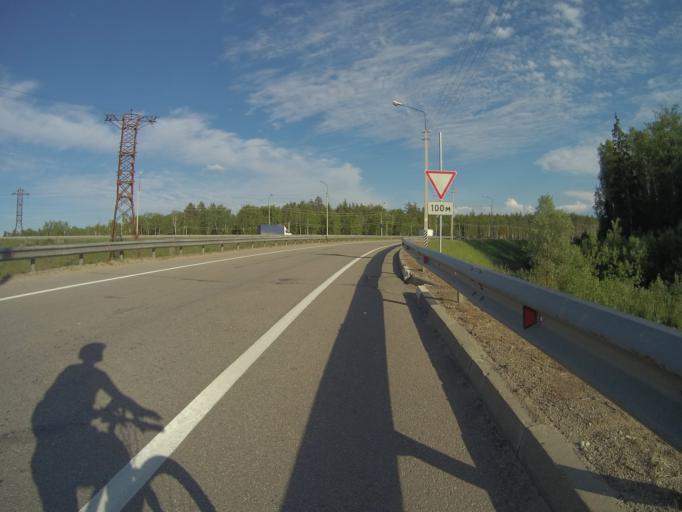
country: RU
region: Vladimir
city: Kameshkovo
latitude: 56.1936
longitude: 40.9502
